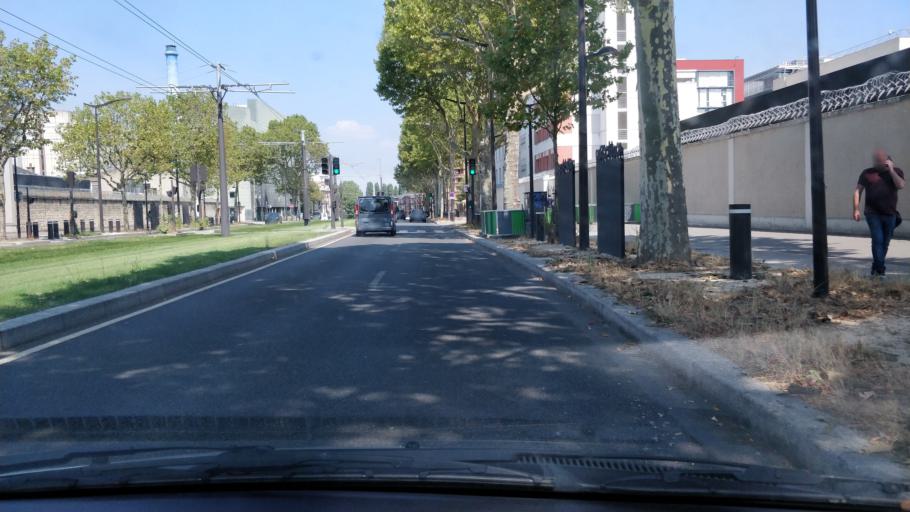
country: FR
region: Ile-de-France
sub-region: Departement de Seine-Saint-Denis
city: Bagnolet
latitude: 48.8743
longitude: 2.4082
